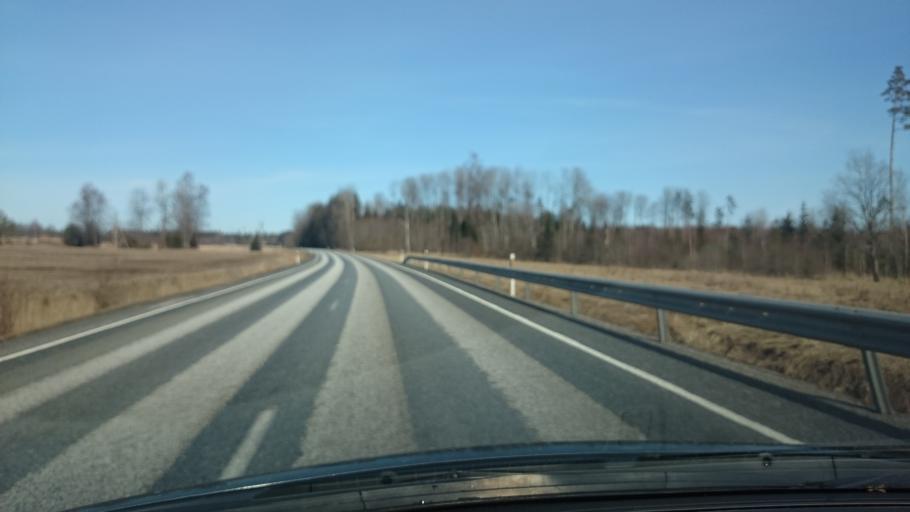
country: EE
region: Jaervamaa
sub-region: Tueri vald
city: Sarevere
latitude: 58.7211
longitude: 25.2796
